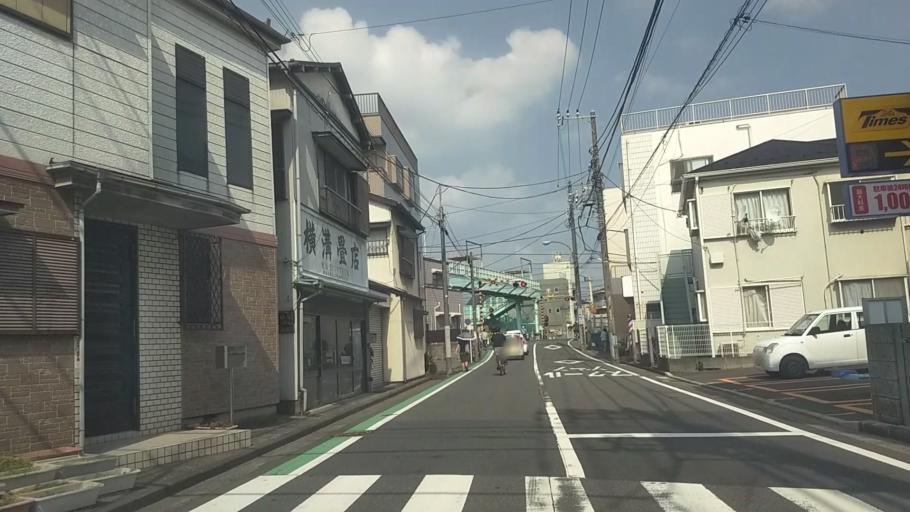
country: JP
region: Kanagawa
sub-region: Kawasaki-shi
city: Kawasaki
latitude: 35.5203
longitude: 139.6853
